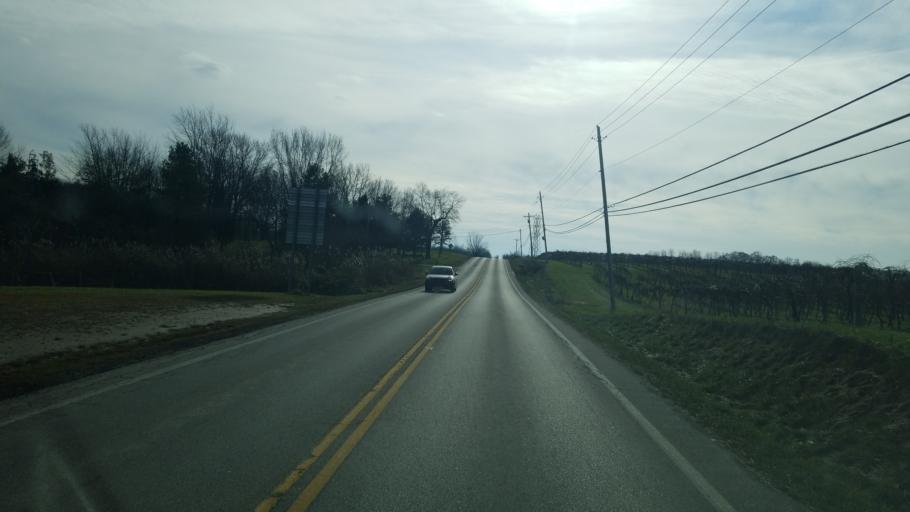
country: US
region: Ohio
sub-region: Ashtabula County
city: Geneva
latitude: 41.7392
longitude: -80.9525
